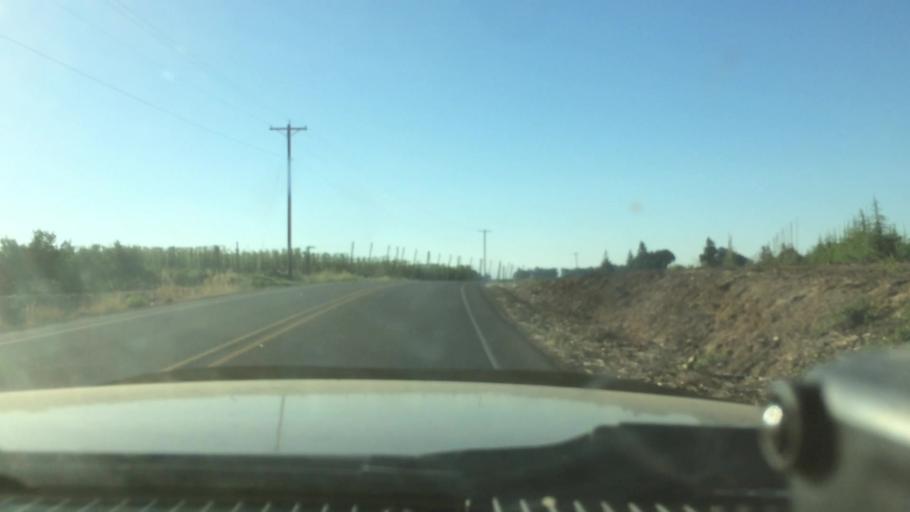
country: US
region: Oregon
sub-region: Marion County
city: Gervais
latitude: 45.1262
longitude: -122.9908
